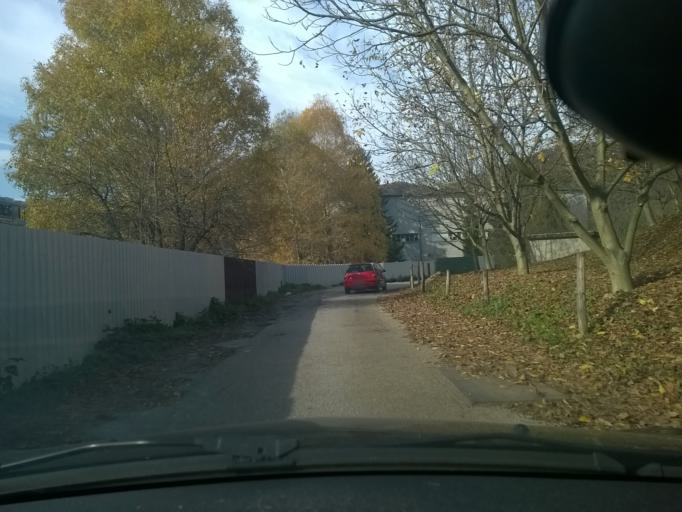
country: HR
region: Krapinsko-Zagorska
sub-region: Grad Krapina
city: Krapina
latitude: 46.1813
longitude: 15.8588
